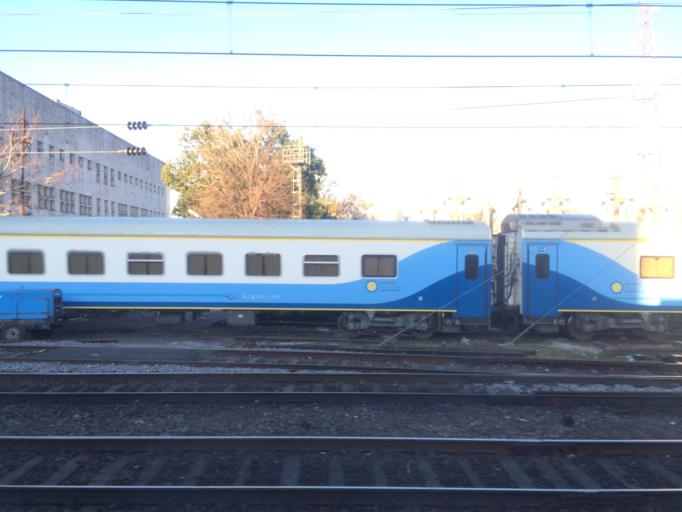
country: AR
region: Buenos Aires F.D.
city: Buenos Aires
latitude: -34.6371
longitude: -58.3806
